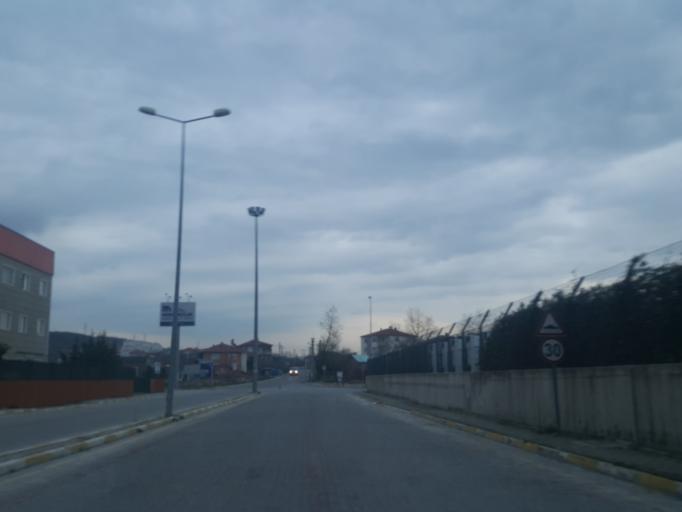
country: TR
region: Kocaeli
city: Tavsanli
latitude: 40.8623
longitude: 29.5704
